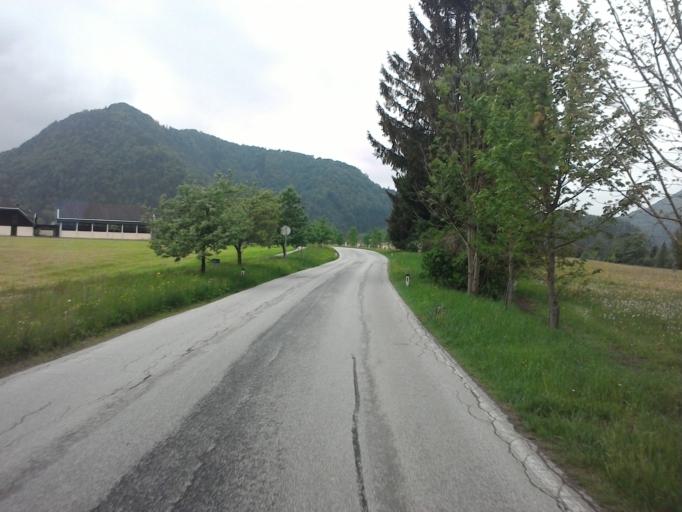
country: AT
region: Styria
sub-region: Politischer Bezirk Liezen
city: Landl
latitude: 47.6553
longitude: 14.7407
